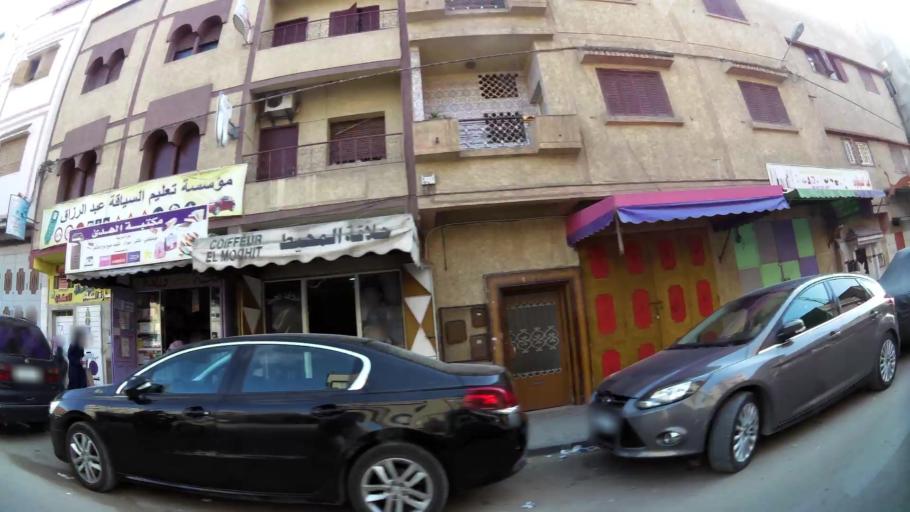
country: MA
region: Rabat-Sale-Zemmour-Zaer
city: Sale
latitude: 34.0513
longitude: -6.7784
